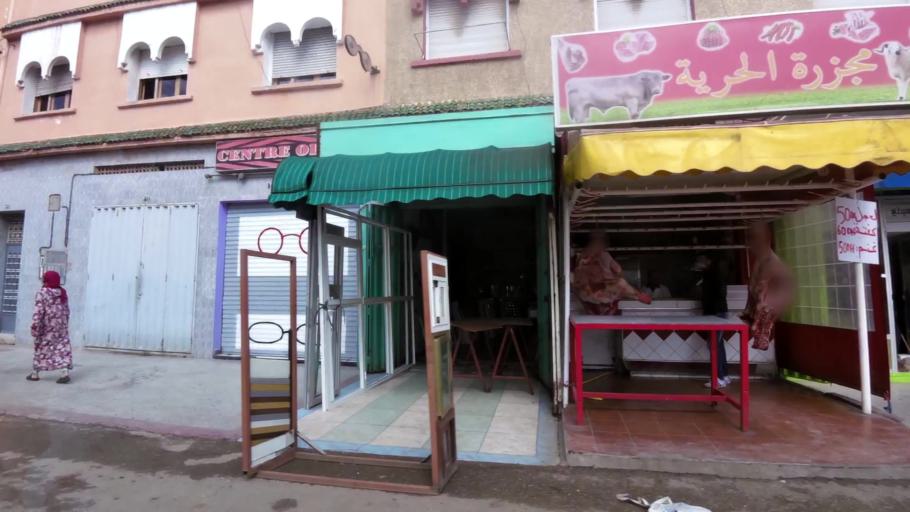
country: MA
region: Chaouia-Ouardigha
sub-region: Settat Province
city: Berrechid
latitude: 33.2659
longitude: -7.5797
